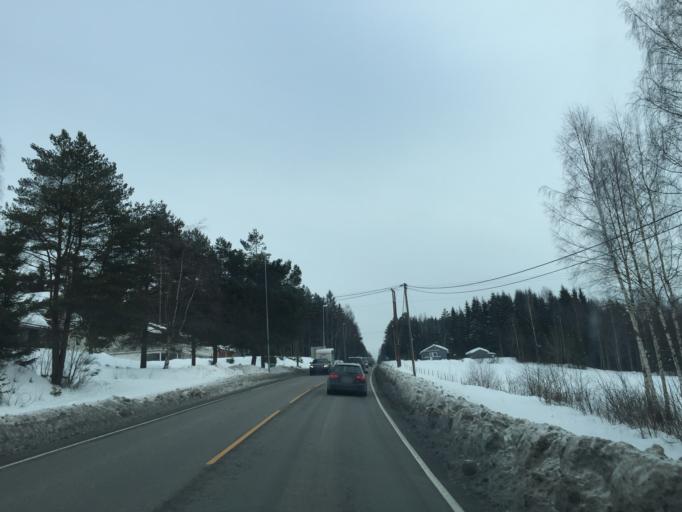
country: NO
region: Hedmark
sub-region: Loten
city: Loten
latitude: 60.8140
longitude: 11.3098
